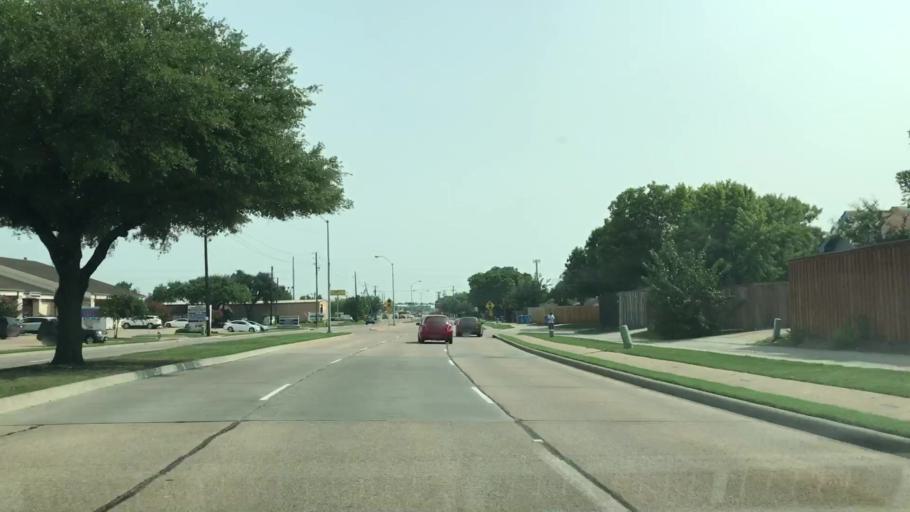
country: US
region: Texas
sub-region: Dallas County
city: Rowlett
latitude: 32.9129
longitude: -96.5696
